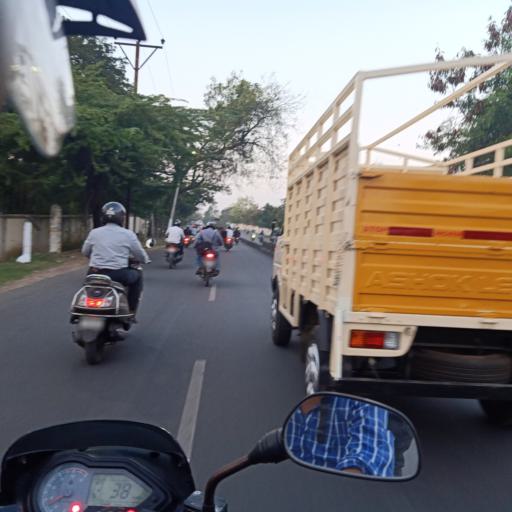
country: IN
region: Telangana
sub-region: Hyderabad
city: Malkajgiri
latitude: 17.4801
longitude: 78.5110
